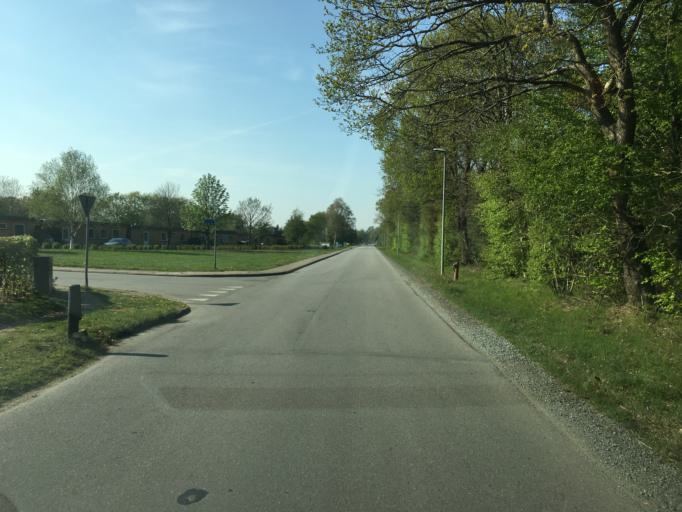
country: DK
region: South Denmark
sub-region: Haderslev Kommune
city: Vojens
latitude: 55.2437
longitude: 9.3181
